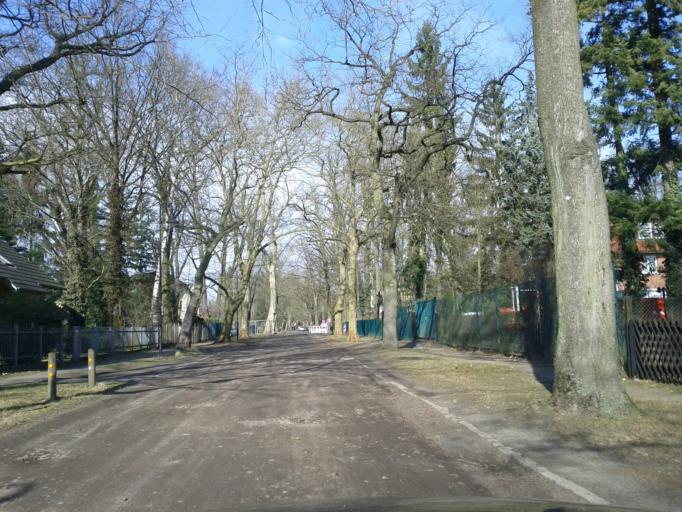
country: DE
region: Brandenburg
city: Schoneiche
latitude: 52.4682
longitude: 13.6933
